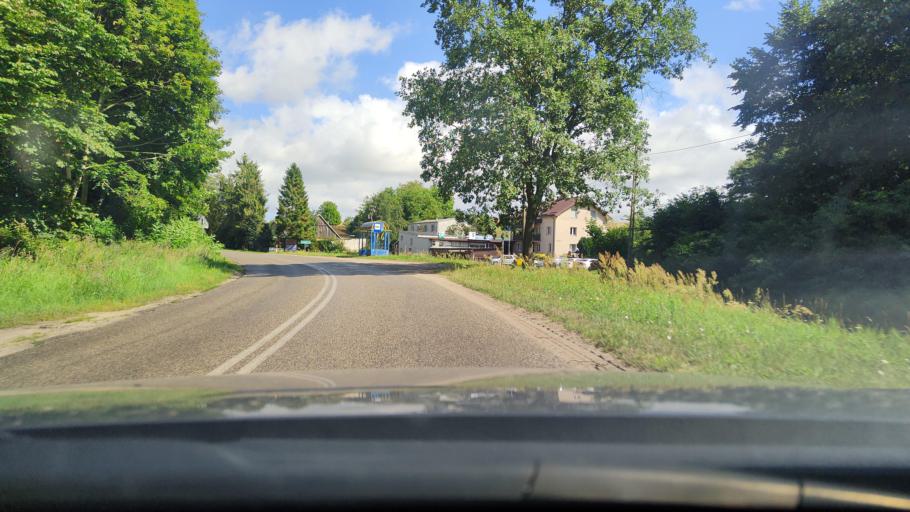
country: PL
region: Pomeranian Voivodeship
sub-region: Powiat pucki
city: Krokowa
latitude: 54.7516
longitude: 18.1743
